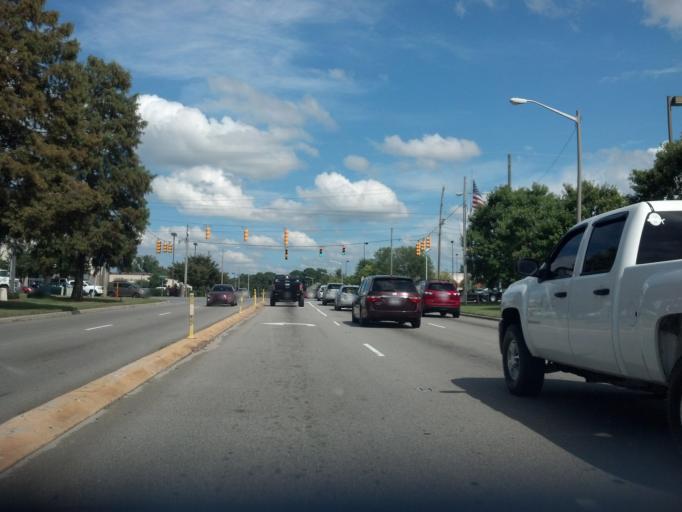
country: US
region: North Carolina
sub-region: Pitt County
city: Windsor
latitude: 35.5666
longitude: -77.3517
